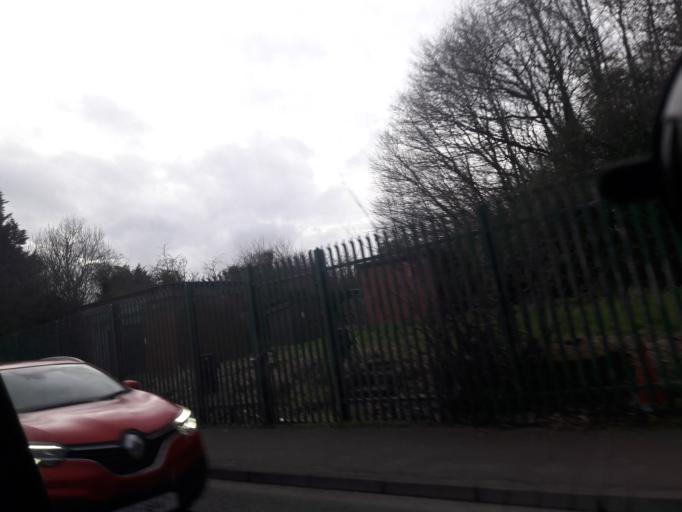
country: GB
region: Northern Ireland
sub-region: City of Belfast
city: Belfast
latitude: 54.6239
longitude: -5.9495
